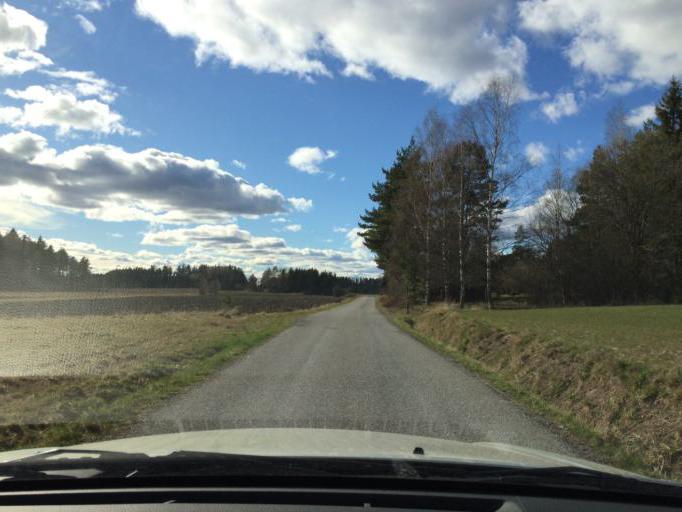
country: SE
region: Soedermanland
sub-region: Eskilstuna Kommun
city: Hallbybrunn
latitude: 59.4294
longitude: 16.3842
